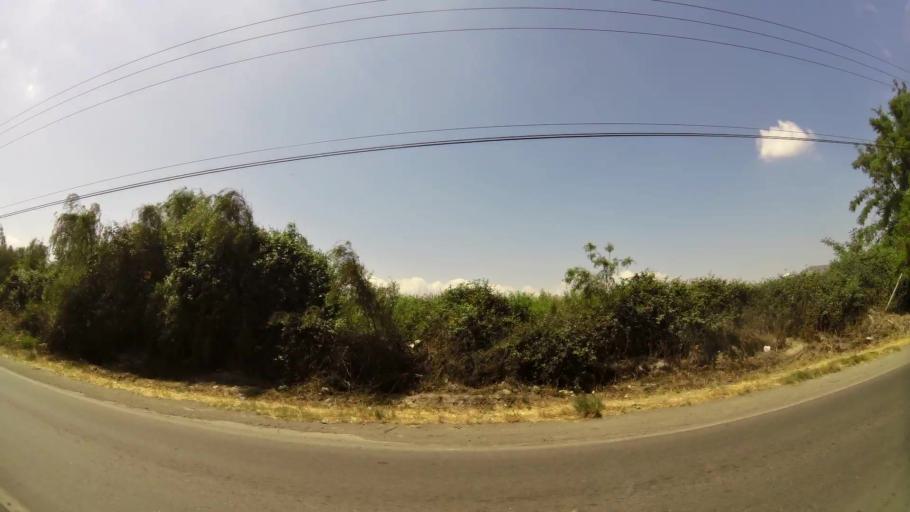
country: CL
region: Santiago Metropolitan
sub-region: Provincia de Maipo
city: San Bernardo
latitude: -33.5406
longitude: -70.7404
